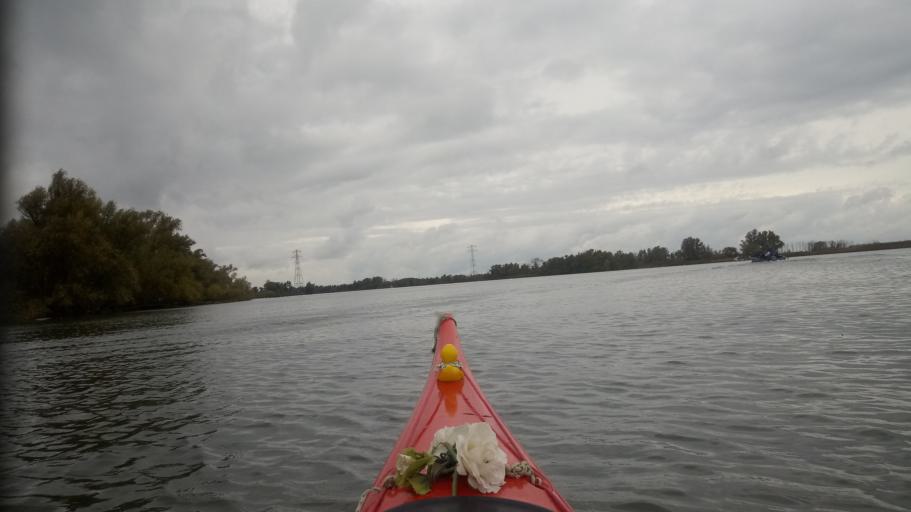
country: NL
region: North Brabant
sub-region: Gemeente Made en Drimmelen
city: Drimmelen
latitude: 51.7555
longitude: 4.8150
